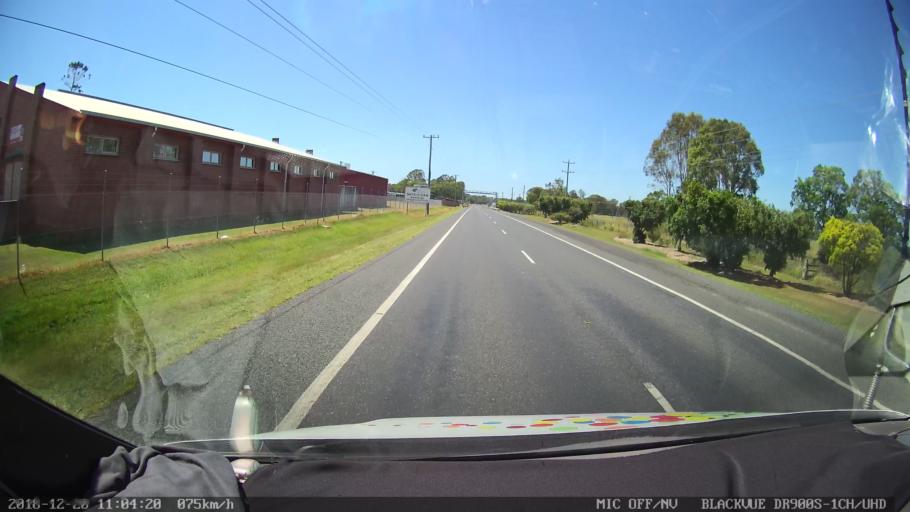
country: AU
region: New South Wales
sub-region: Richmond Valley
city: Casino
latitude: -28.8841
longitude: 153.0450
